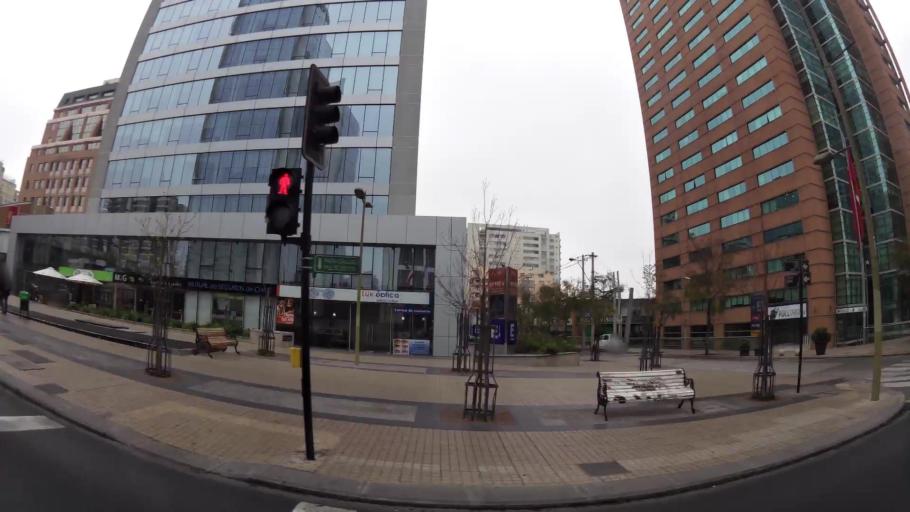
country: CL
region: Santiago Metropolitan
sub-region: Provincia de Santiago
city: Villa Presidente Frei, Nunoa, Santiago, Chile
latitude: -33.4123
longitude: -70.5794
